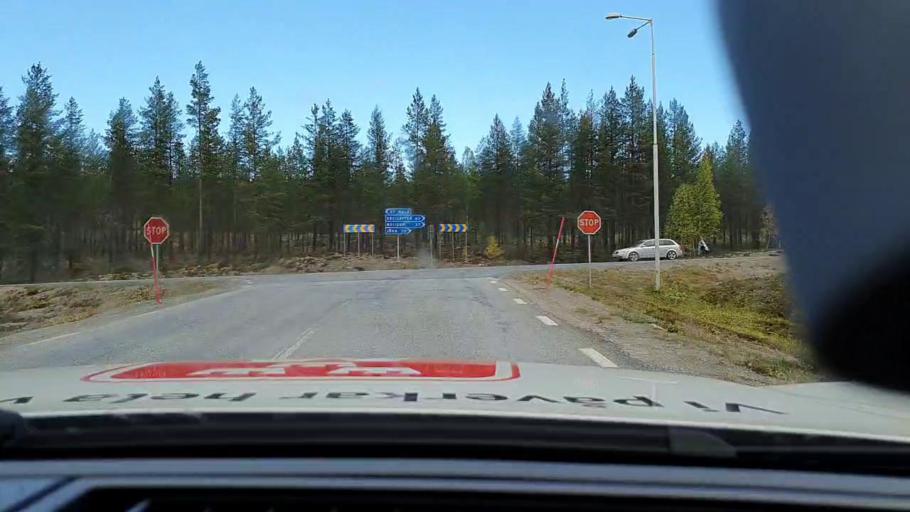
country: SE
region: Vaesterbotten
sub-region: Norsjo Kommun
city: Norsjoe
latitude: 64.9736
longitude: 19.7175
